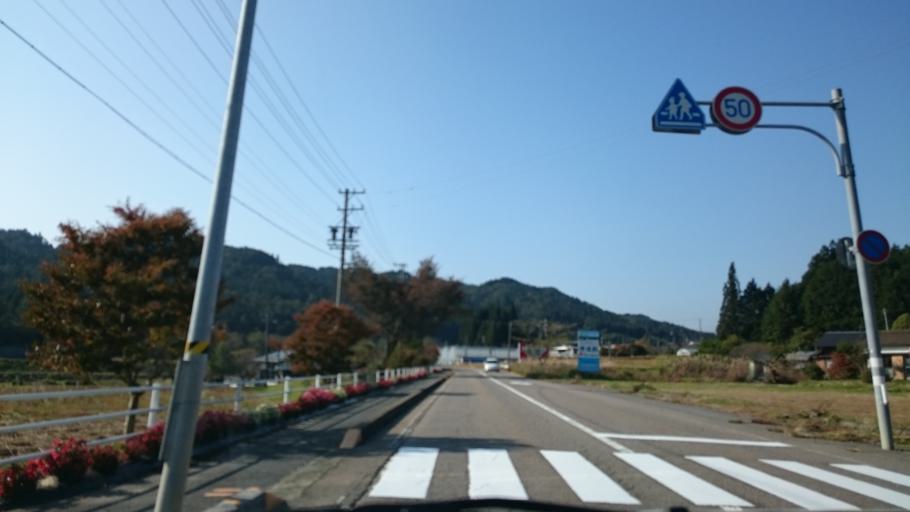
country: JP
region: Gifu
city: Nakatsugawa
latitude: 35.7440
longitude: 137.3370
